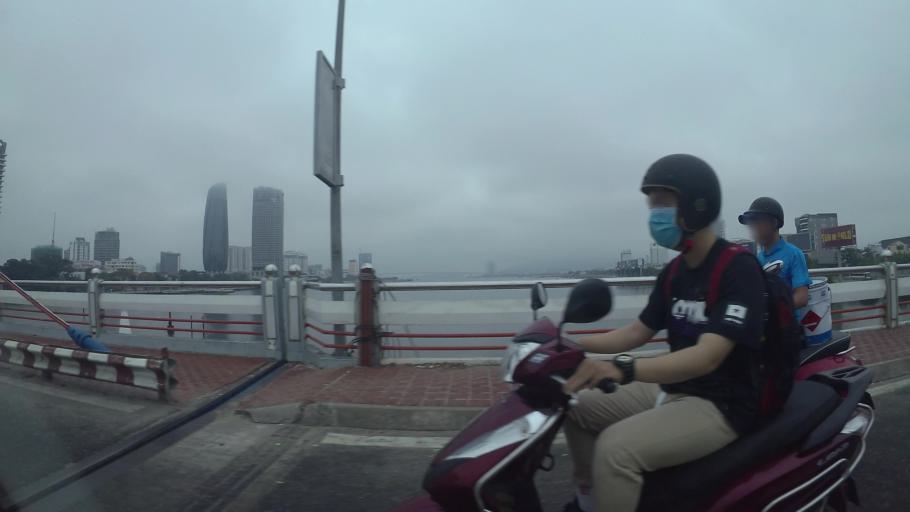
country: VN
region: Da Nang
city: Da Nang
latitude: 16.0725
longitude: 108.2276
